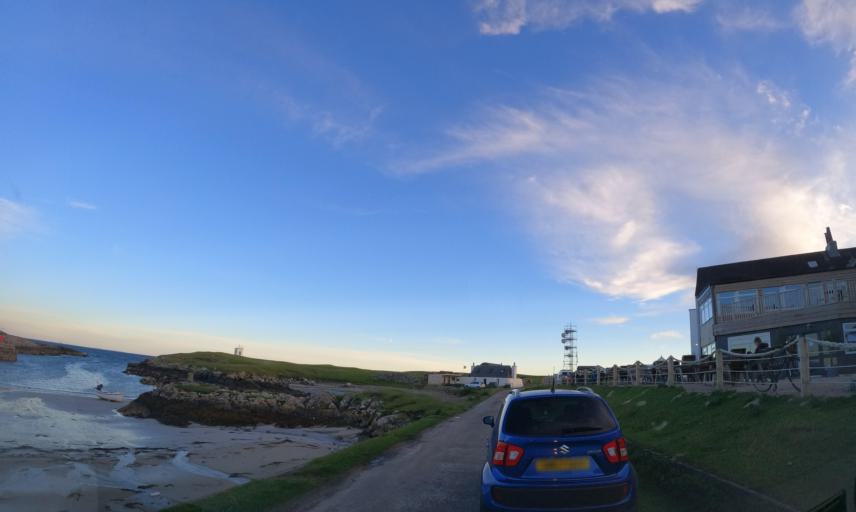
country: GB
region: Scotland
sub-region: Eilean Siar
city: Barra
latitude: 56.5016
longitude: -6.8060
